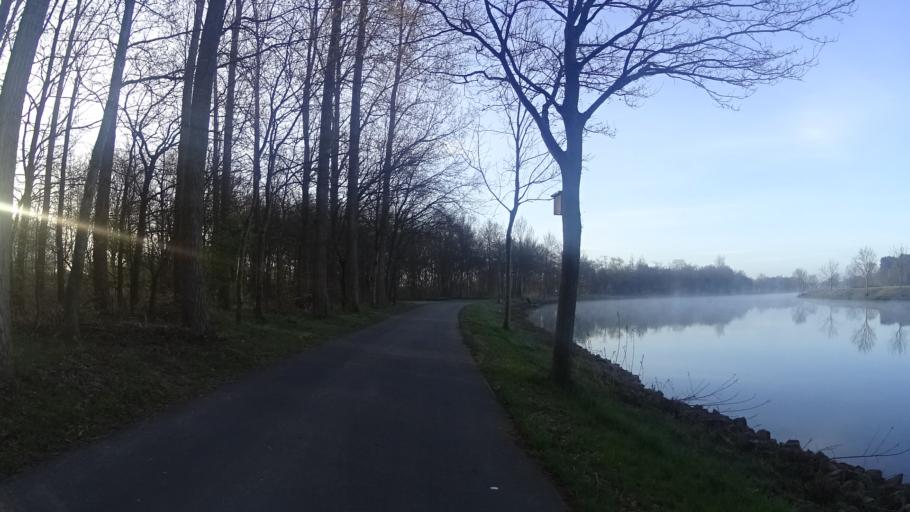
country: DE
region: Lower Saxony
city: Sustrum
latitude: 52.9119
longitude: 7.3128
